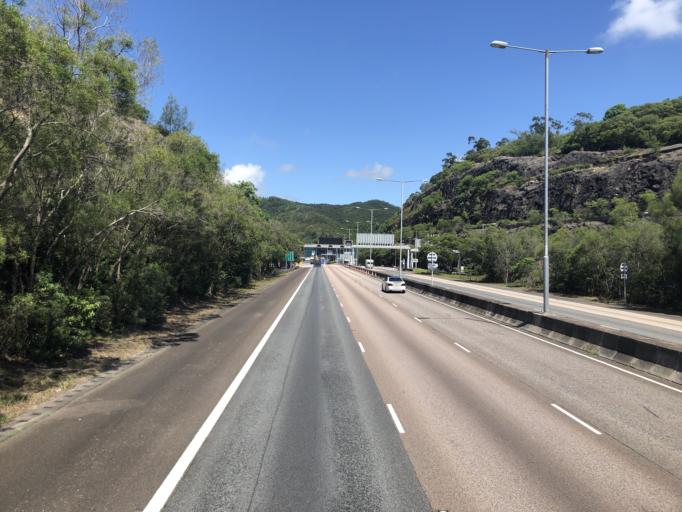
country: HK
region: Tsuen Wan
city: Tsuen Wan
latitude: 22.3718
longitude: 114.0729
